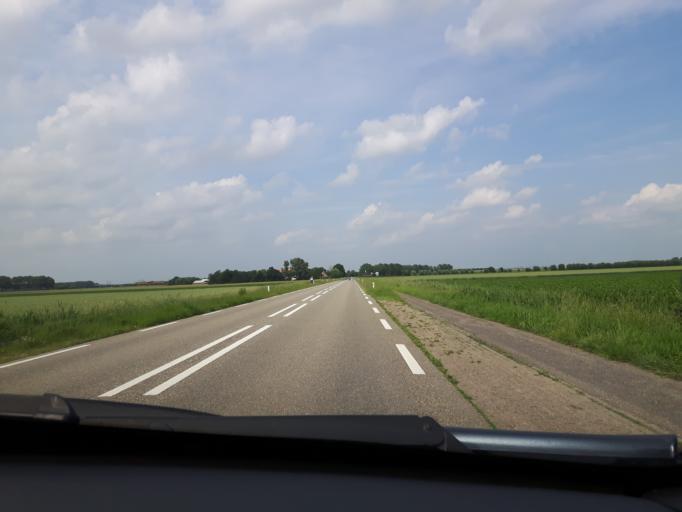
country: NL
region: Zeeland
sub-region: Gemeente Veere
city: Veere
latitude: 51.4952
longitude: 3.6874
